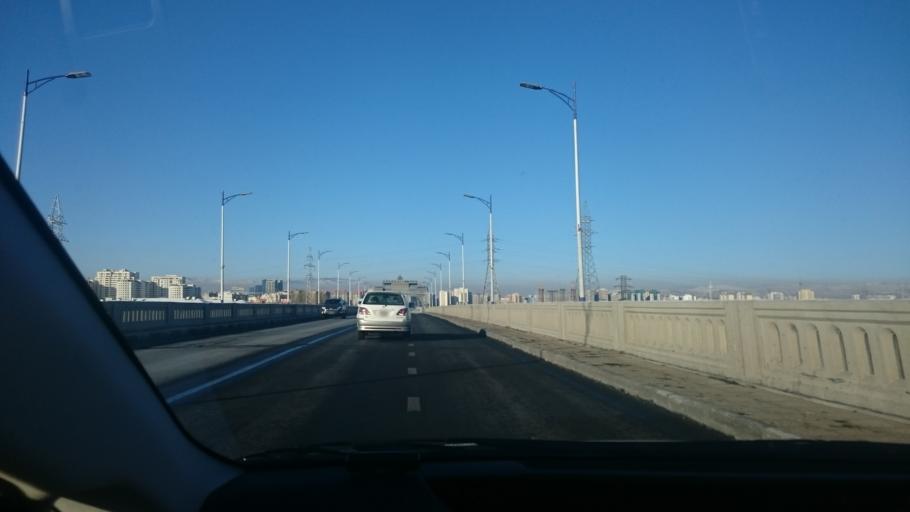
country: MN
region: Ulaanbaatar
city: Ulaanbaatar
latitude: 47.8868
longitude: 106.9399
